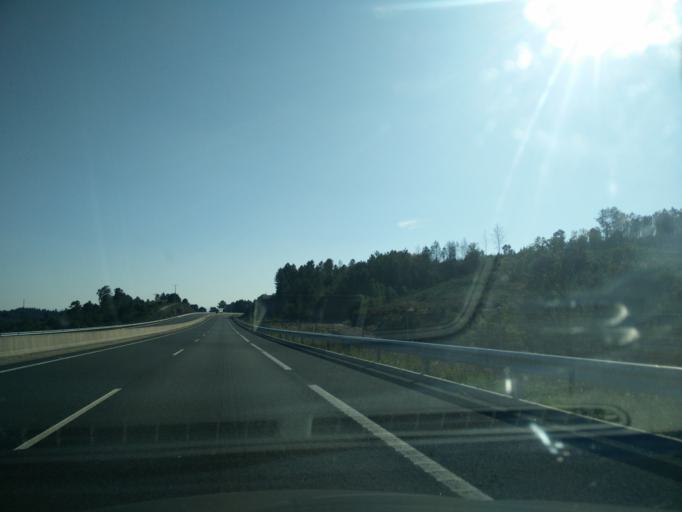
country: ES
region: Galicia
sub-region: Provincia de Ourense
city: Pinor
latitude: 42.5092
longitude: -8.0224
